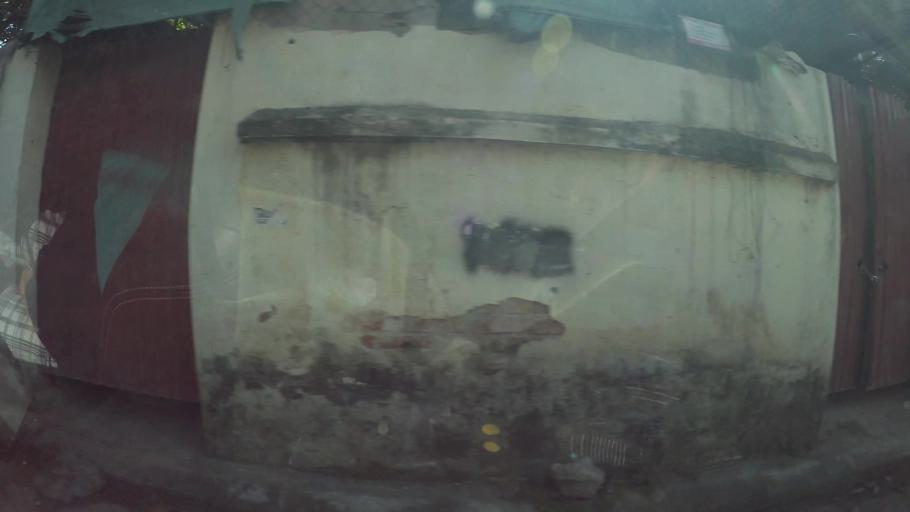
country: VN
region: Ha Noi
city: Hoan Kiem
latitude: 21.0647
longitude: 105.8698
